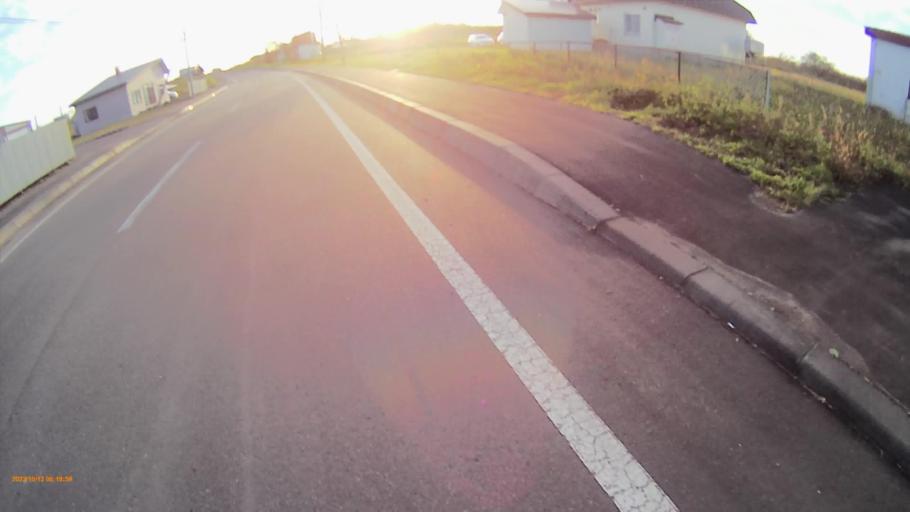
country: JP
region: Hokkaido
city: Kushiro
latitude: 42.8857
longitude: 143.9293
